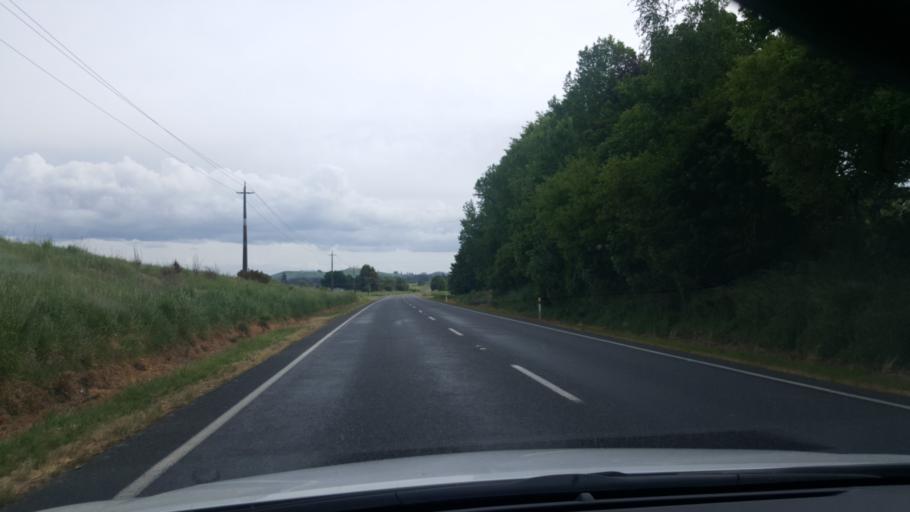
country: NZ
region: Bay of Plenty
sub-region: Rotorua District
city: Rotorua
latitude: -38.3947
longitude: 176.3367
